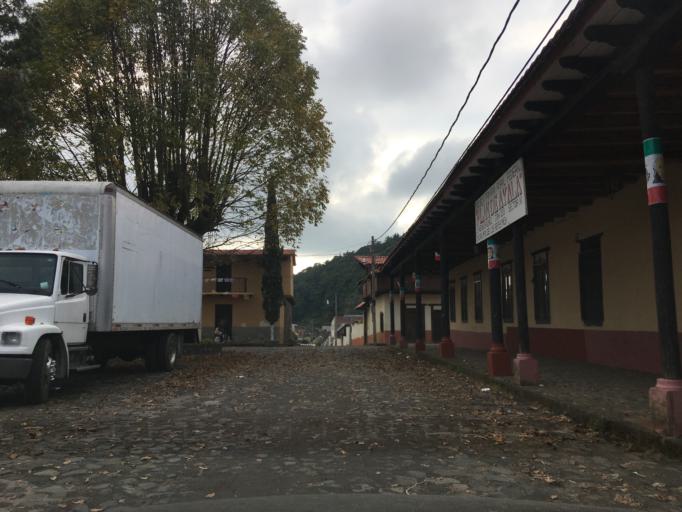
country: MX
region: Michoacan
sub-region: Uruapan
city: Santa Ana Zirosto
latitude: 19.5655
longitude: -102.2876
